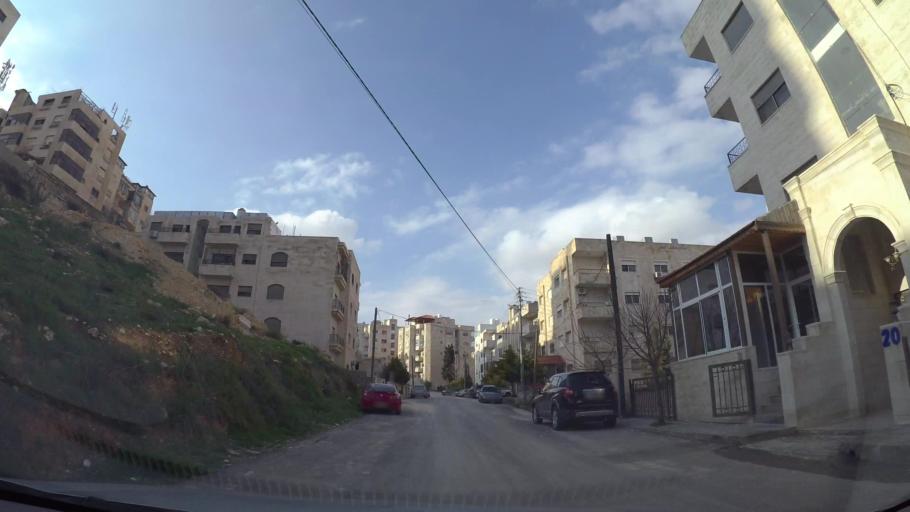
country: JO
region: Amman
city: Al Jubayhah
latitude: 32.0051
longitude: 35.8638
